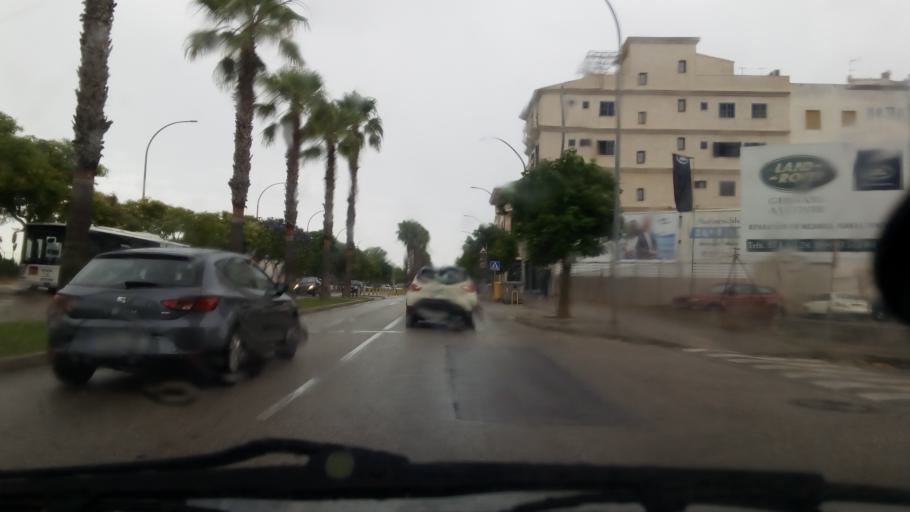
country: ES
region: Balearic Islands
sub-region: Illes Balears
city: Manacor
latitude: 39.5689
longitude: 3.2196
